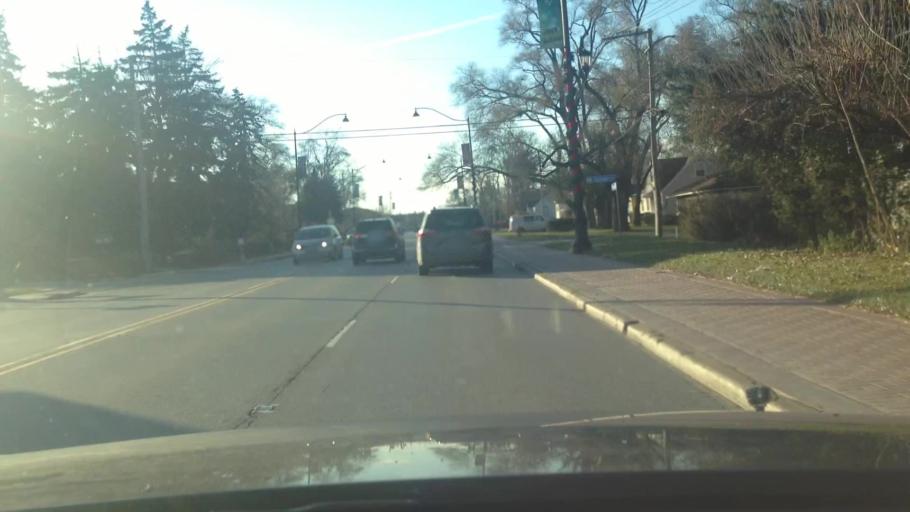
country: US
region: Illinois
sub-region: DuPage County
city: Bensenville
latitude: 41.9610
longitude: -87.9522
